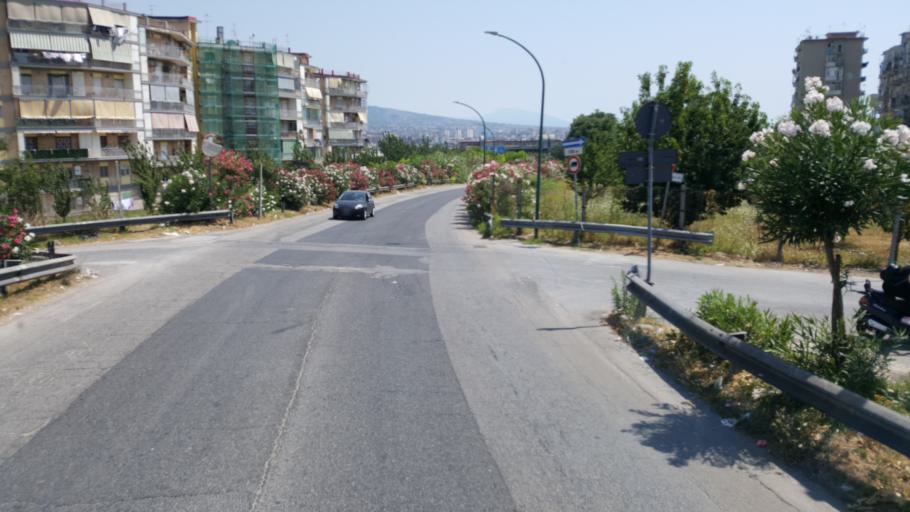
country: IT
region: Campania
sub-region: Provincia di Napoli
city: Arpino
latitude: 40.8835
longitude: 14.3163
